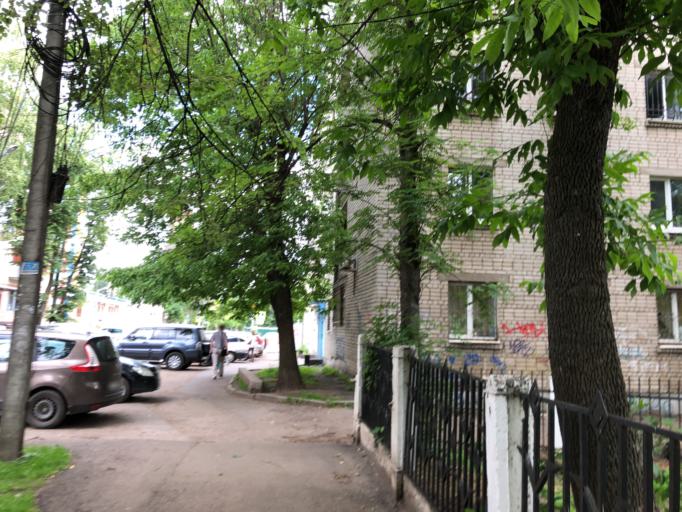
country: RU
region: Jaroslavl
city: Yaroslavl
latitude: 57.6233
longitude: 39.8666
